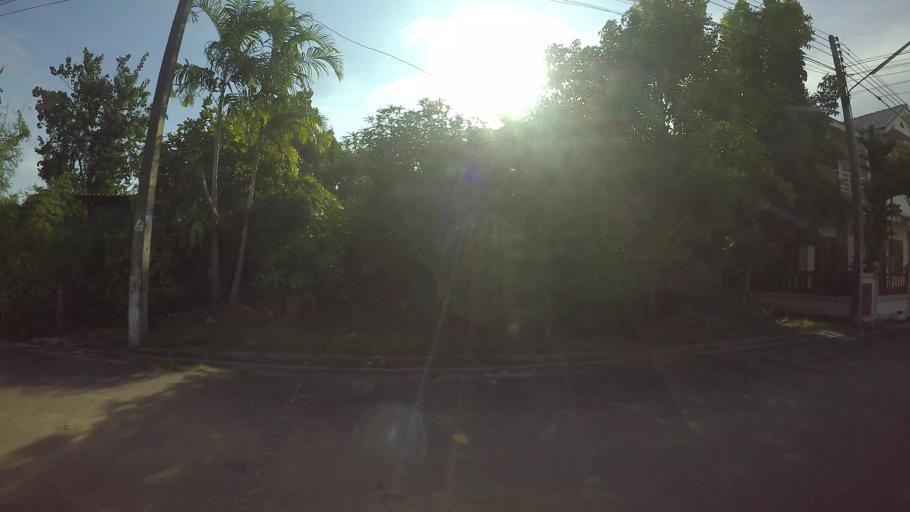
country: TH
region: Rayong
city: Rayong
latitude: 12.6938
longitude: 101.2749
